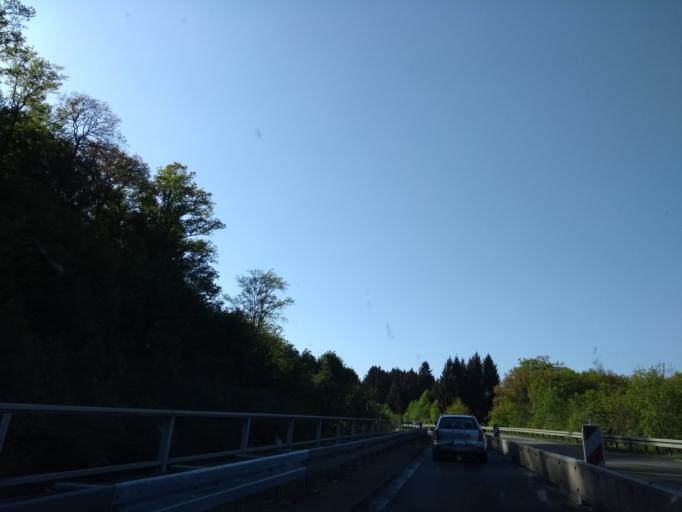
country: DE
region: Hesse
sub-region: Regierungsbezirk Giessen
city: Biedenkopf
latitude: 50.9227
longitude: 8.4995
